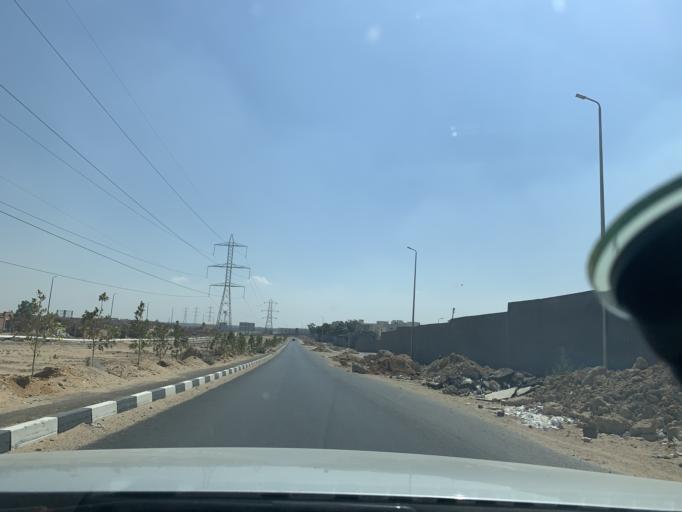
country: EG
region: Muhafazat al Qahirah
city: Cairo
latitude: 30.0314
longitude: 31.3503
